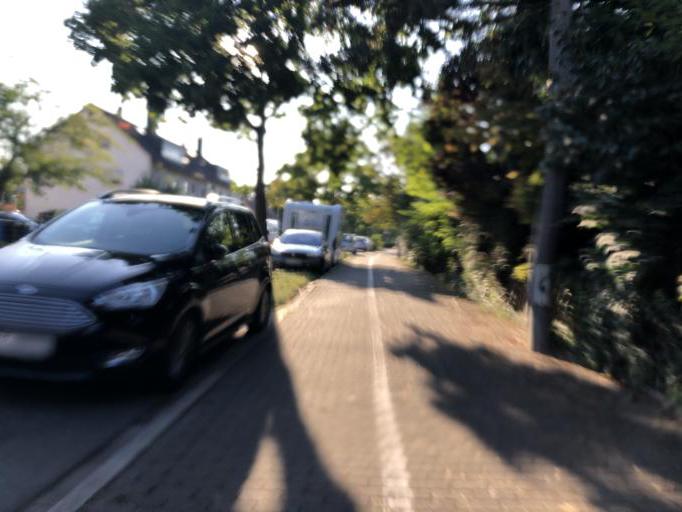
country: DE
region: Bavaria
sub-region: Regierungsbezirk Mittelfranken
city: Erlangen
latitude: 49.5926
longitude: 10.9665
